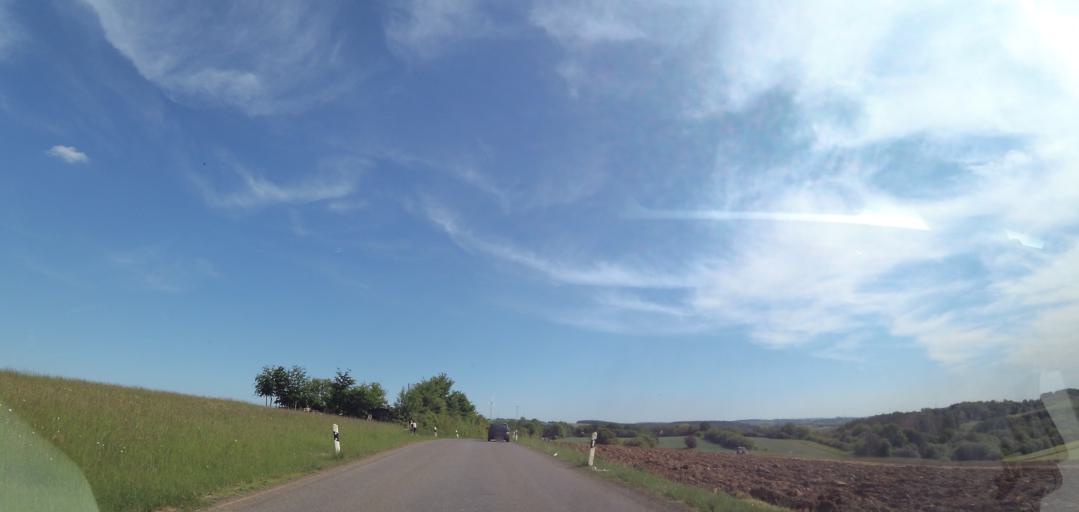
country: DE
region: Saarland
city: Eppelborn
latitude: 49.4568
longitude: 6.9552
